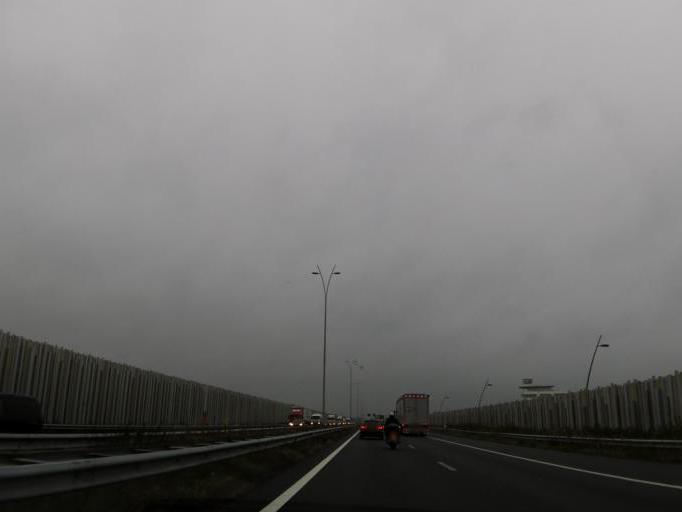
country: NL
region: North Brabant
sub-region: Gemeente Eindhoven
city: Meerhoven
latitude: 51.4244
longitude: 5.4283
